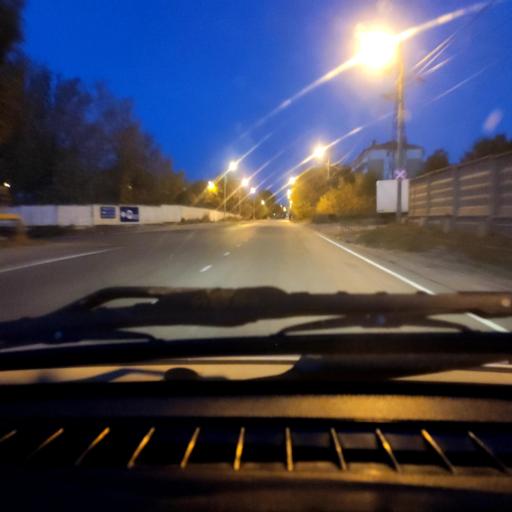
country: RU
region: Samara
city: Zhigulevsk
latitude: 53.4644
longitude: 49.5427
